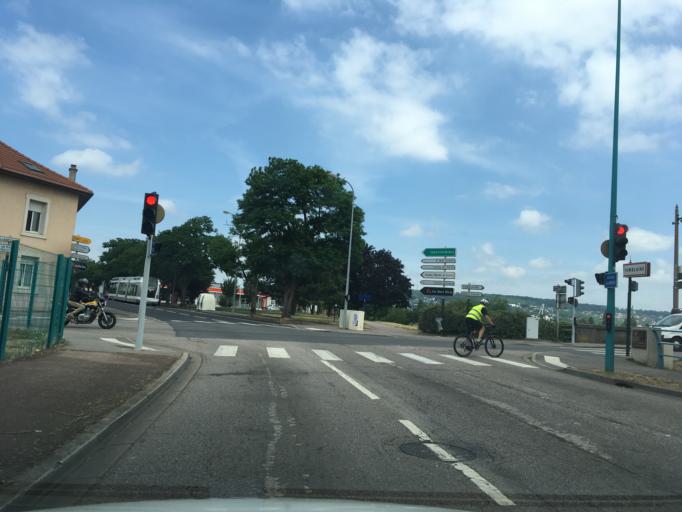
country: FR
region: Lorraine
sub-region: Departement de Meurthe-et-Moselle
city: Tomblaine
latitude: 48.6874
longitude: 6.2057
